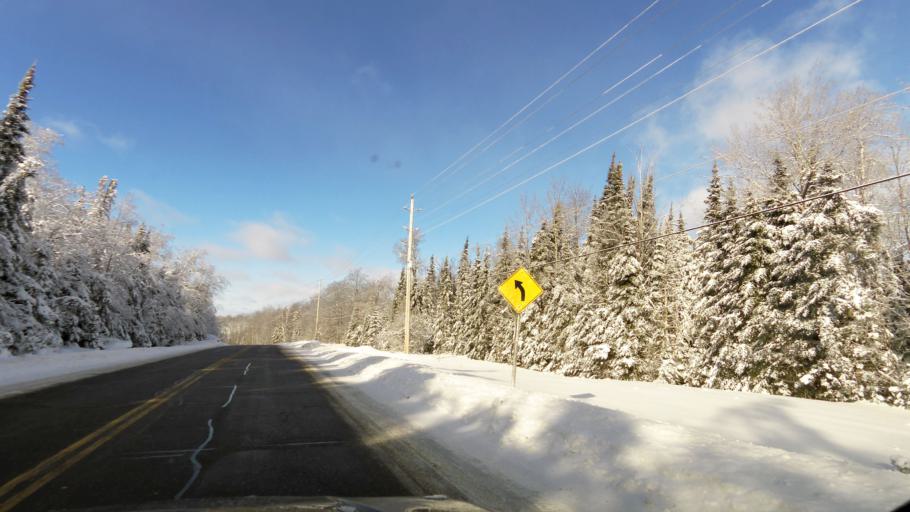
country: CA
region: Ontario
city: Bancroft
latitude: 45.0077
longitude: -78.3088
